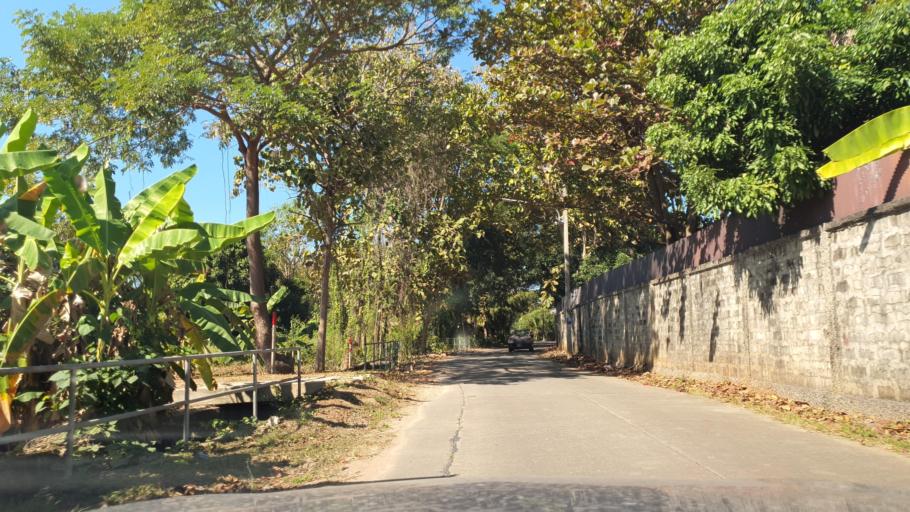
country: TH
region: Chiang Mai
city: Hang Dong
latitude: 18.6797
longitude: 98.9267
